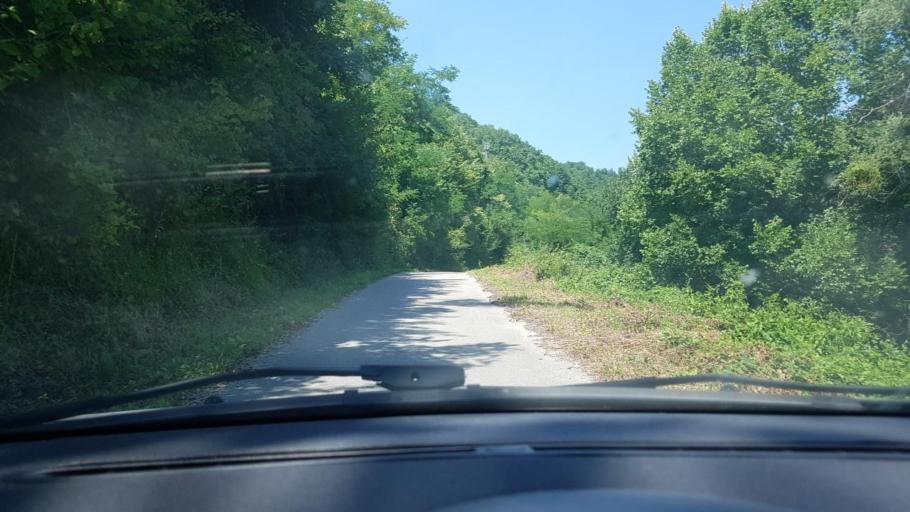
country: BA
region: Federation of Bosnia and Herzegovina
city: Orasac
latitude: 44.5619
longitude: 16.0824
